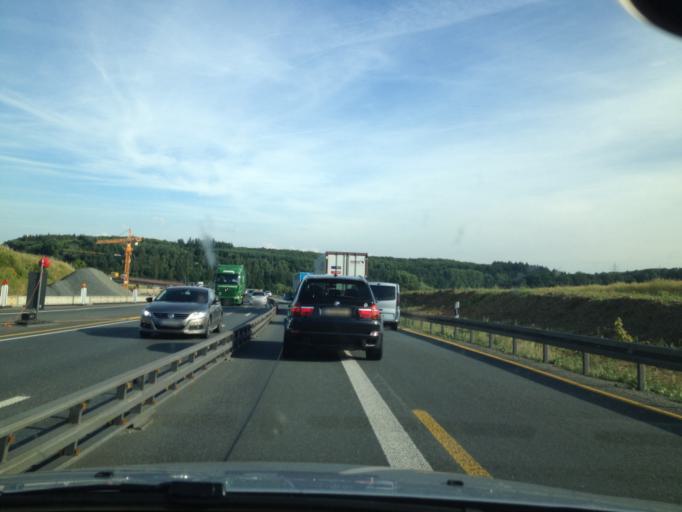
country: DE
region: Hesse
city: Allendorf an der Lahn
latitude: 50.5511
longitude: 8.5649
